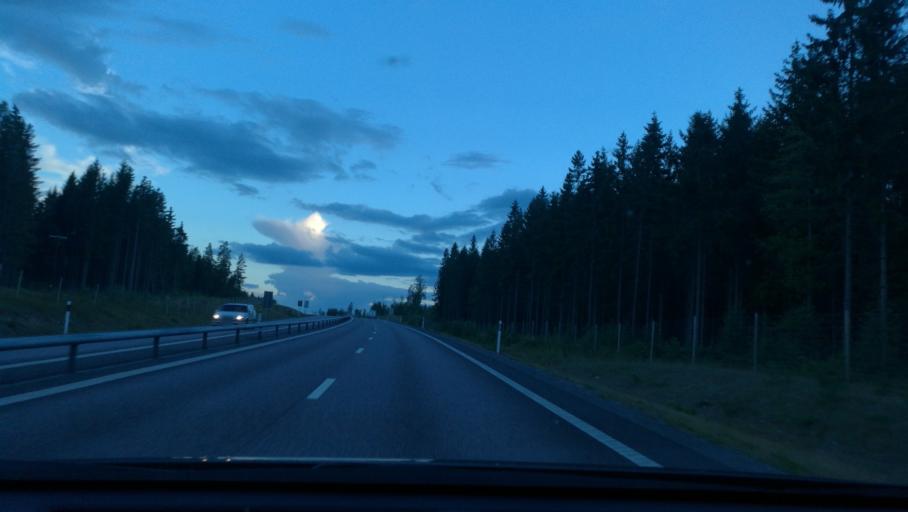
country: SE
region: Soedermanland
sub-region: Katrineholms Kommun
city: Katrineholm
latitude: 58.9556
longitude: 16.2232
